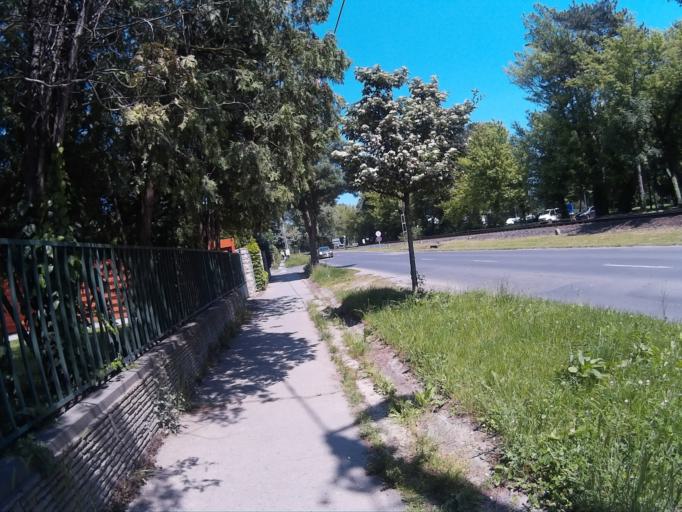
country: HU
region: Zala
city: Keszthely
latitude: 46.7612
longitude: 17.2515
